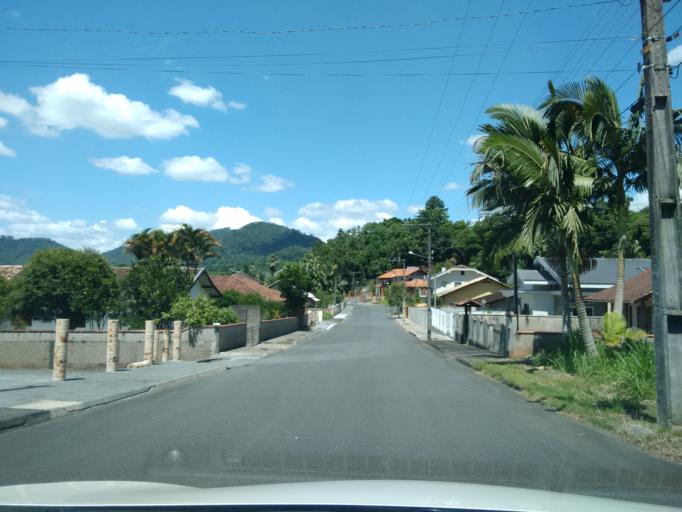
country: BR
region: Santa Catarina
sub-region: Pomerode
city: Pomerode
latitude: -26.7565
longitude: -49.1798
